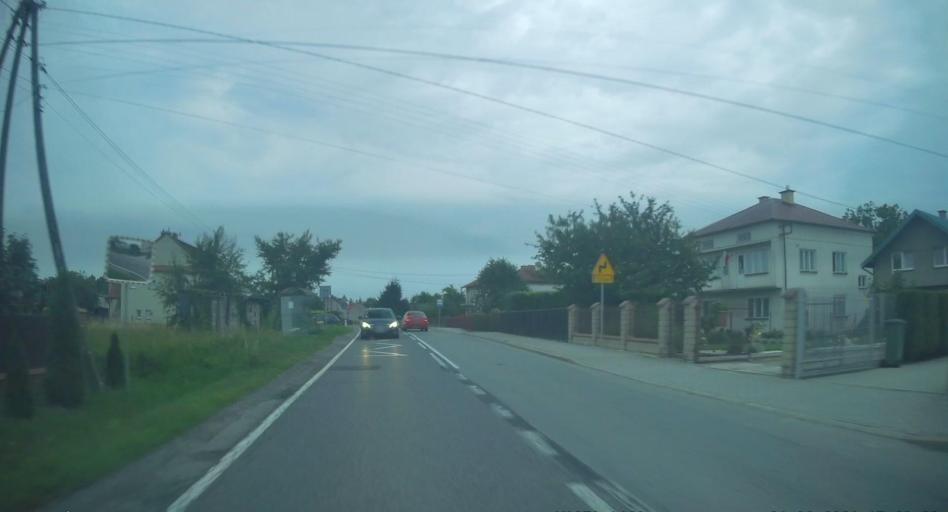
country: PL
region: Lesser Poland Voivodeship
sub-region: Powiat tarnowski
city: Wierzchoslawice
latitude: 49.9979
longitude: 20.8538
